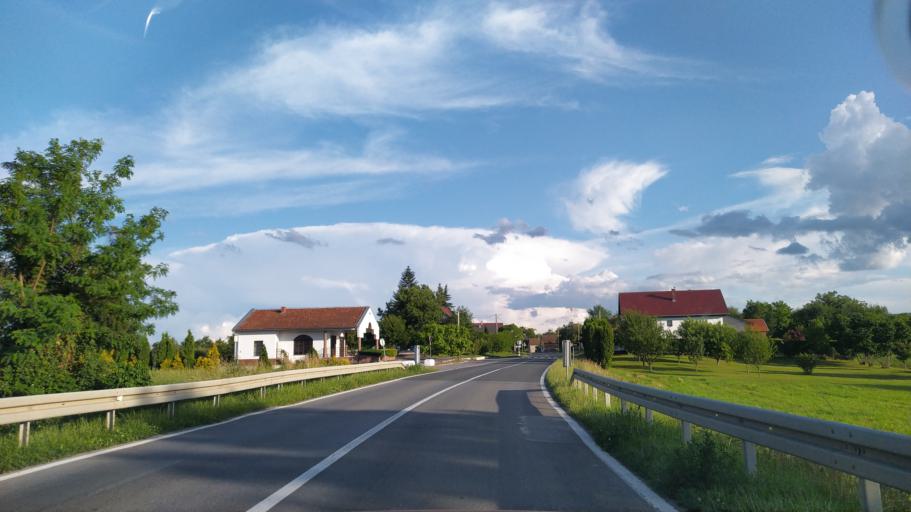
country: HR
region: Virovitick-Podravska
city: Cacinci
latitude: 45.6218
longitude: 17.8019
